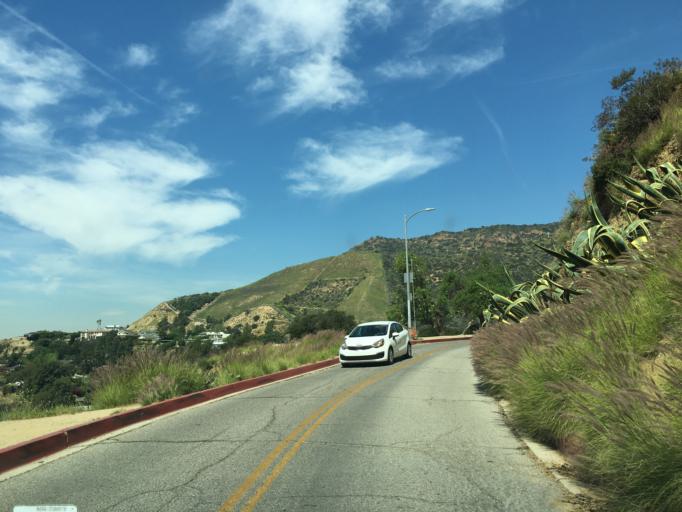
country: US
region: California
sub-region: Los Angeles County
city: Hollywood
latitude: 34.1272
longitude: -118.3247
